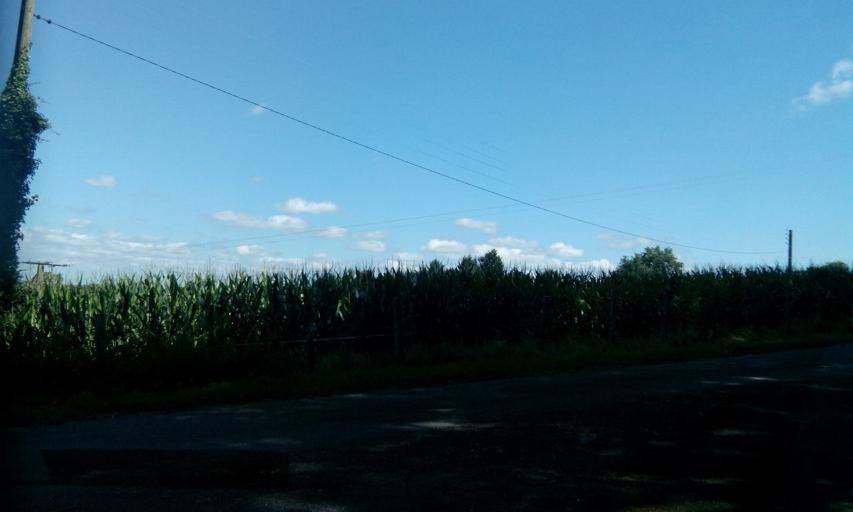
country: FR
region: Limousin
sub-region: Departement de la Haute-Vienne
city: Saint-Leonard-de-Noblat
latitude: 45.8136
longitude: 1.4796
